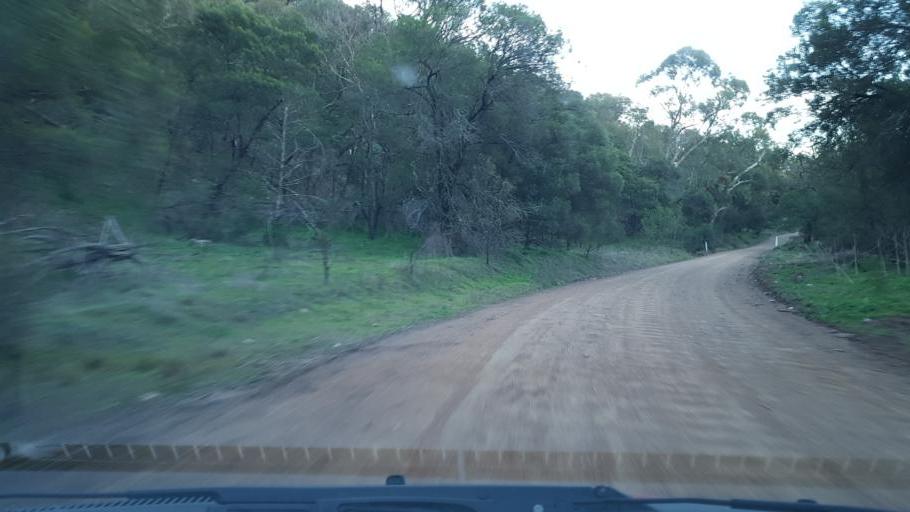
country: AU
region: New South Wales
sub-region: Palerang
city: Bungendore
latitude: -35.1677
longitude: 149.3941
